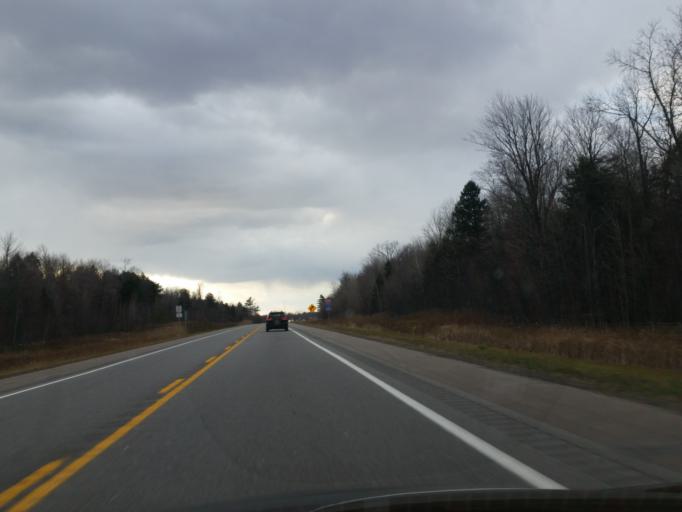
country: CA
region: Quebec
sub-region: Laurentides
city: Lachute
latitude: 45.6442
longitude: -74.2566
